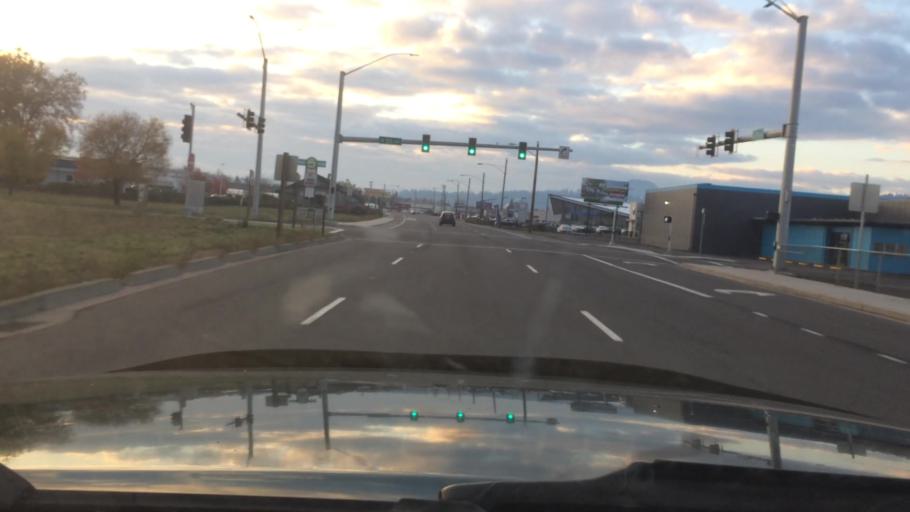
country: US
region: Oregon
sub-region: Lane County
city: Eugene
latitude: 44.0553
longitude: -123.1292
